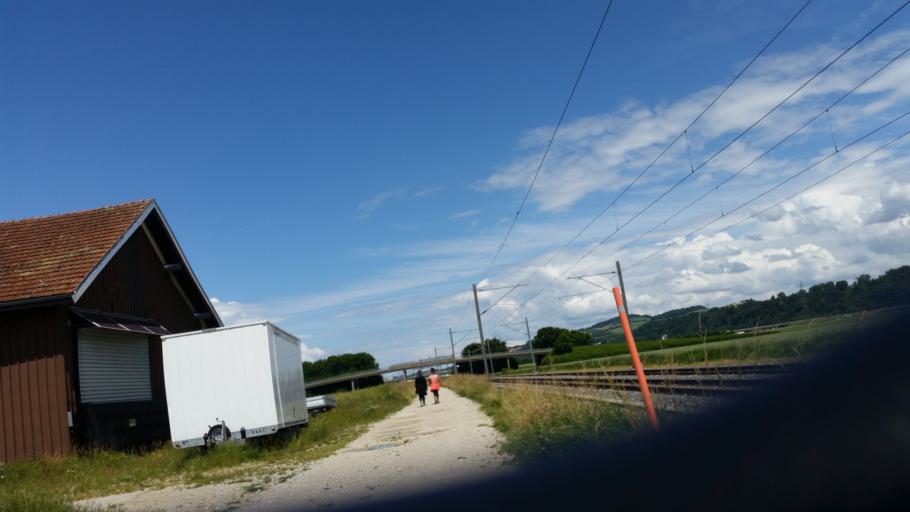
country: CH
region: Vaud
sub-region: Jura-Nord vaudois District
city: Yverdon-les-Bains
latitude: 46.7547
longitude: 6.6216
